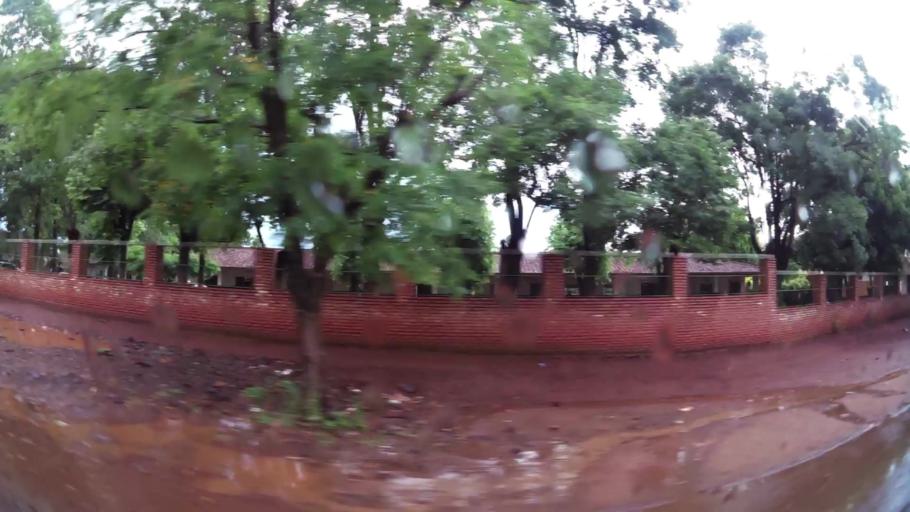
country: PY
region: Alto Parana
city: Presidente Franco
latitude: -25.5576
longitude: -54.6600
